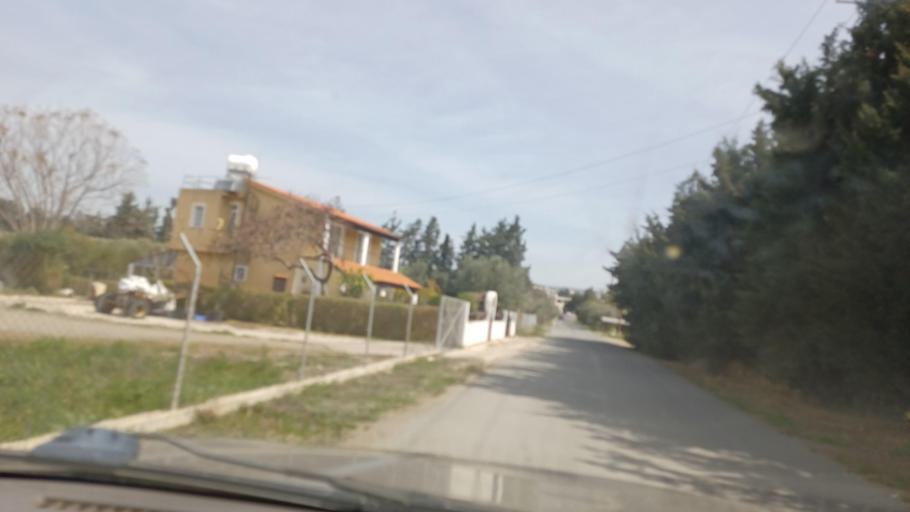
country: CY
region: Pafos
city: Paphos
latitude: 34.7473
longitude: 32.4627
